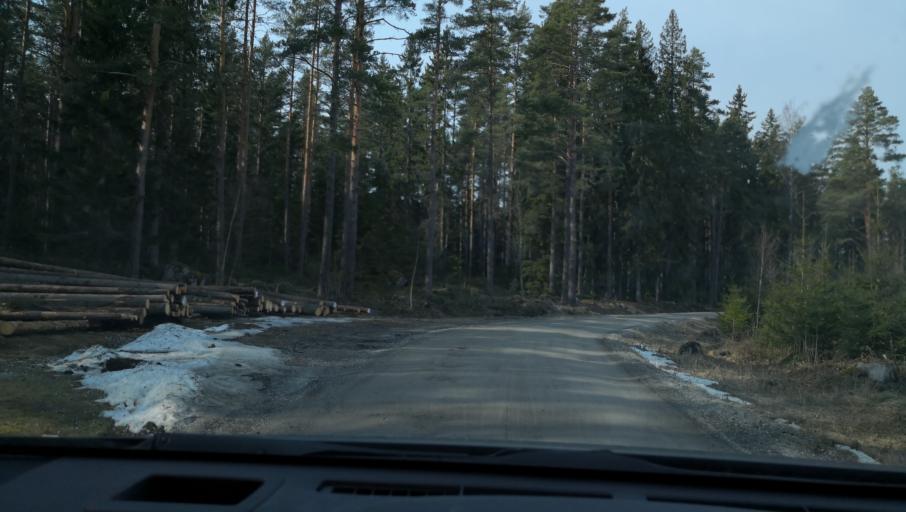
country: SE
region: OErebro
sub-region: Lindesbergs Kommun
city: Frovi
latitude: 59.3603
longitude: 15.4332
